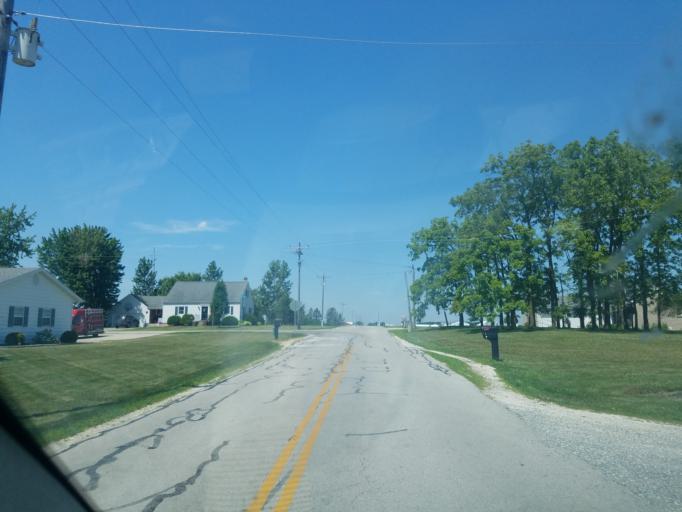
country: US
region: Ohio
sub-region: Mercer County
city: Saint Henry
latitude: 40.4506
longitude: -84.6762
